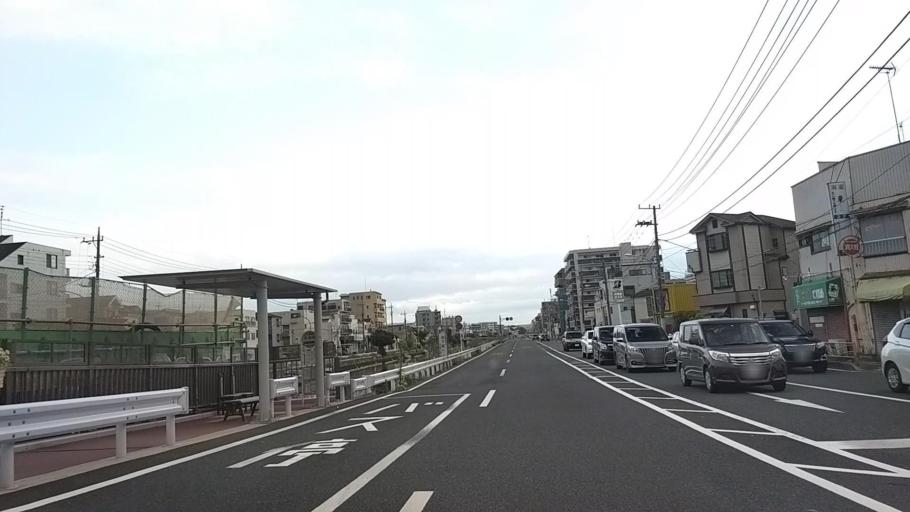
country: JP
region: Kanagawa
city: Yokohama
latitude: 35.4261
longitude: 139.6231
